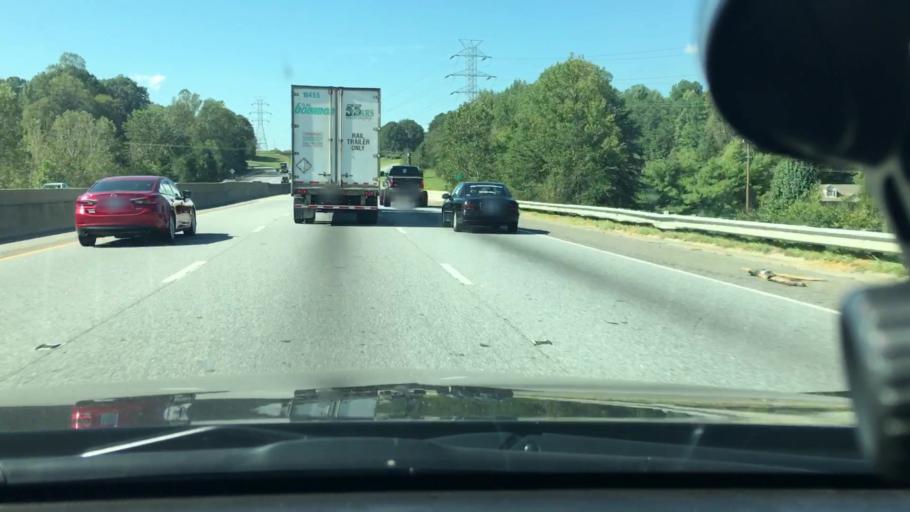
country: US
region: North Carolina
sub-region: Gaston County
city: Bessemer City
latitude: 35.2693
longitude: -81.2505
